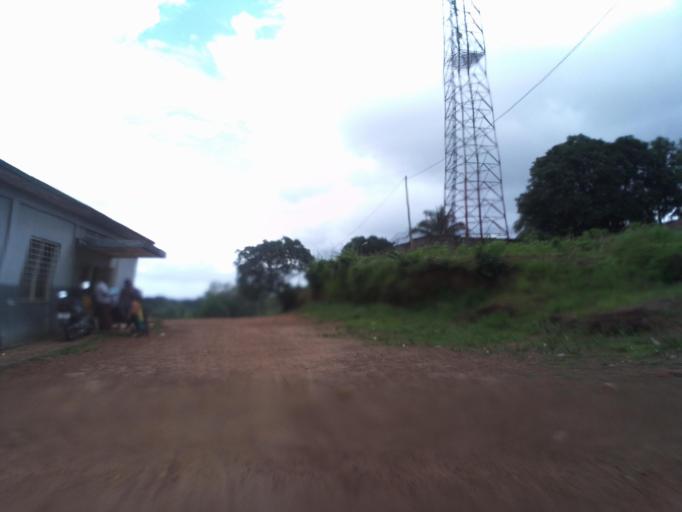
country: SL
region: Eastern Province
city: Kenema
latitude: 7.8592
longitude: -11.1875
